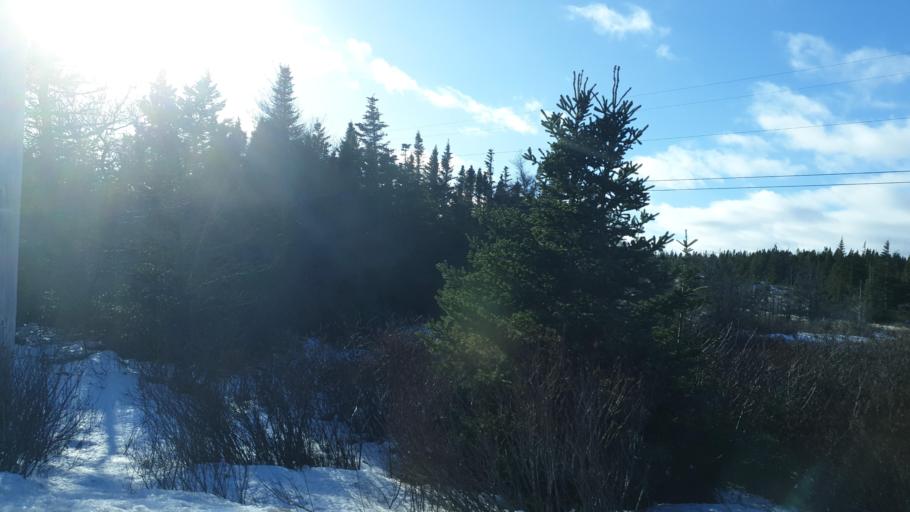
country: CA
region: Newfoundland and Labrador
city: Bonavista
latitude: 48.6288
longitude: -53.0363
